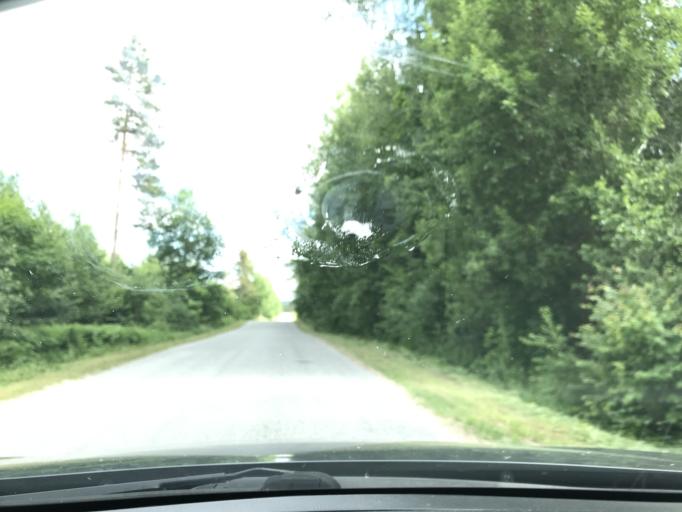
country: LV
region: Alsunga
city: Alsunga
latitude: 56.9933
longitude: 21.6247
